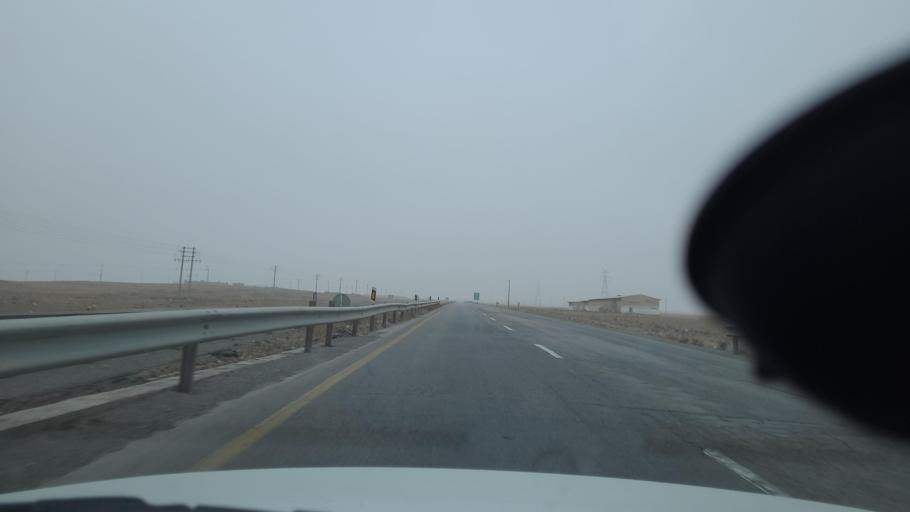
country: IR
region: Razavi Khorasan
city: Fariman
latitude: 35.9008
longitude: 59.7574
